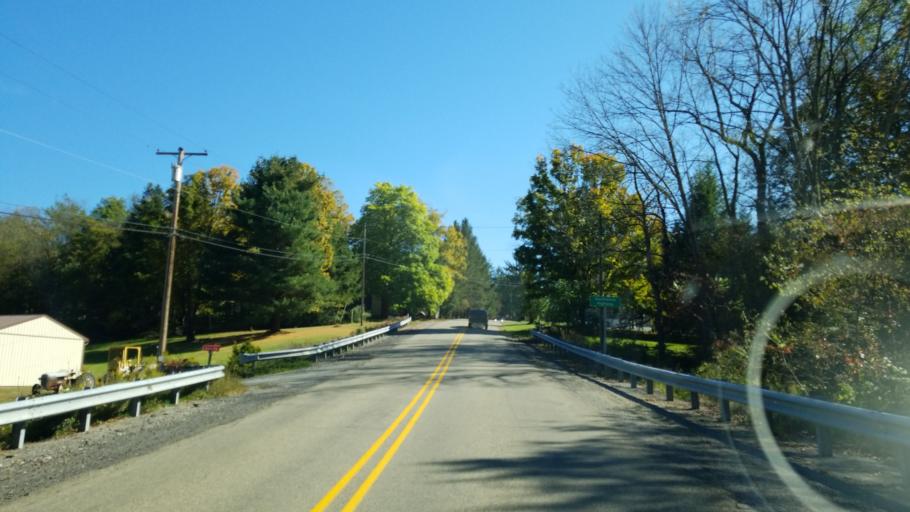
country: US
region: Pennsylvania
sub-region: Elk County
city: Saint Marys
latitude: 41.2884
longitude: -78.3960
